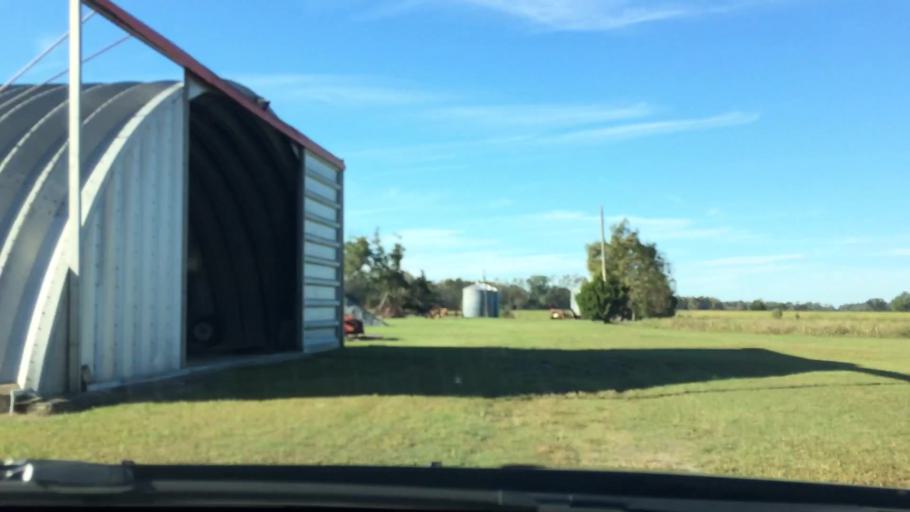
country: US
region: North Carolina
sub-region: Pitt County
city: Ayden
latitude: 35.4754
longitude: -77.4675
